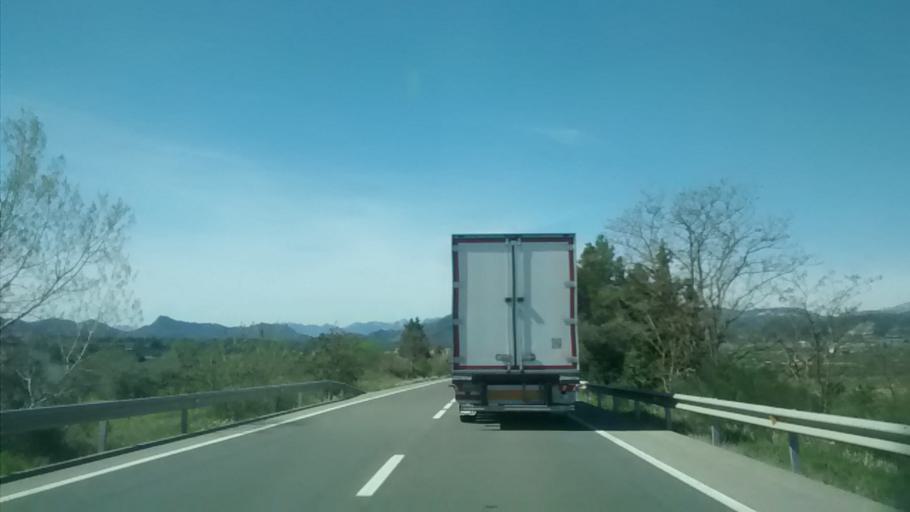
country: ES
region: Catalonia
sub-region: Provincia de Tarragona
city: Ginestar
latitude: 41.0457
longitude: 0.6449
